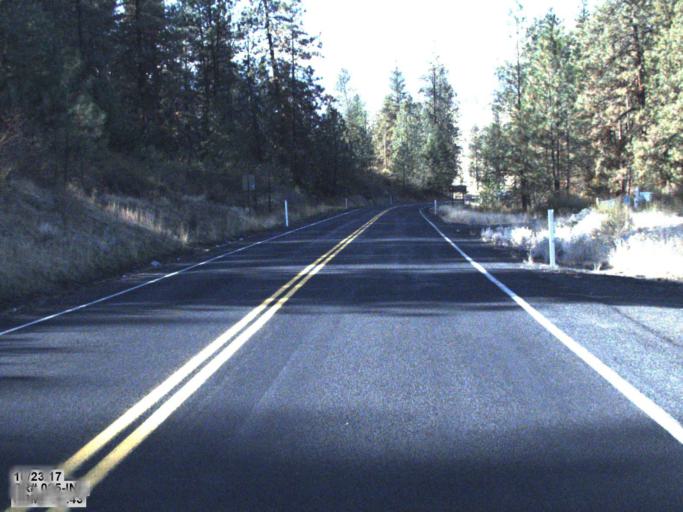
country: US
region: Washington
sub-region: Lincoln County
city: Davenport
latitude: 47.9027
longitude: -118.2993
